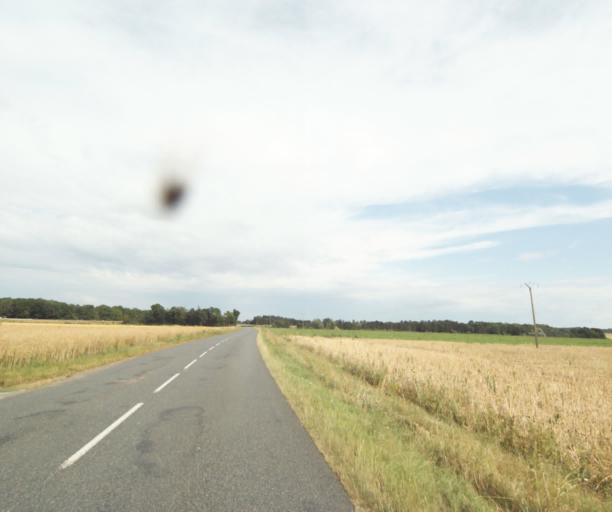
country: FR
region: Ile-de-France
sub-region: Departement de Seine-et-Marne
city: Acheres-la-Foret
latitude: 48.3486
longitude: 2.5833
